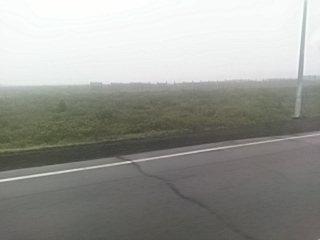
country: RU
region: Krasnoyarskiy
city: Kayyerkan
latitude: 69.3761
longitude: 87.3912
